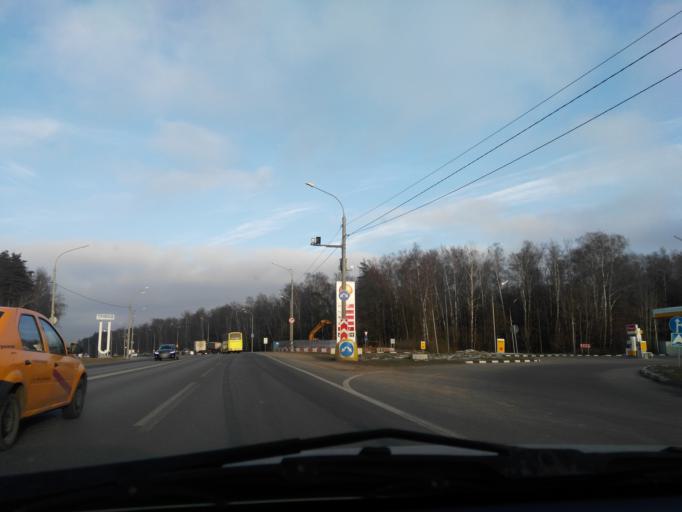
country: RU
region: Moskovskaya
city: Troitsk
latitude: 55.4769
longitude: 37.3166
